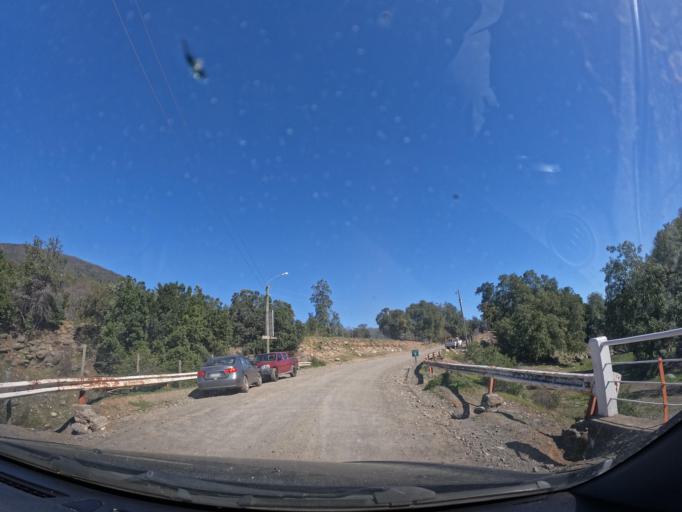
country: CL
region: Maule
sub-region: Provincia de Linares
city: Longavi
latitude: -36.2302
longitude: -71.4021
